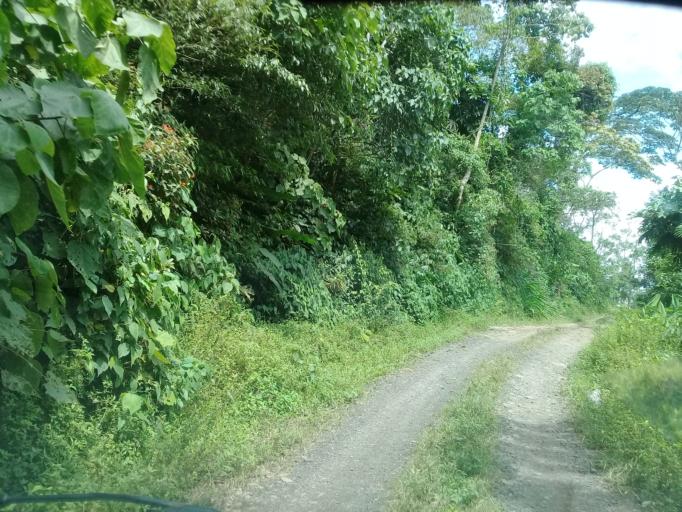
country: CO
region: Cundinamarca
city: Granada
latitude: 5.1151
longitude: -74.5680
